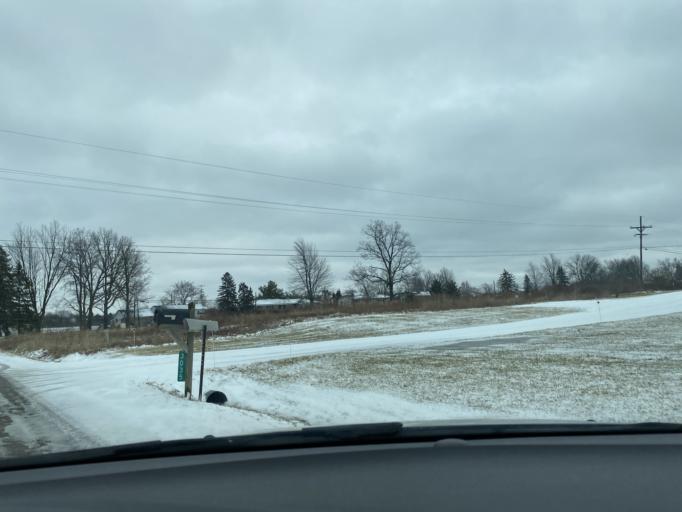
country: US
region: Michigan
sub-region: Lapeer County
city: Lapeer
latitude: 43.0646
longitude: -83.3445
